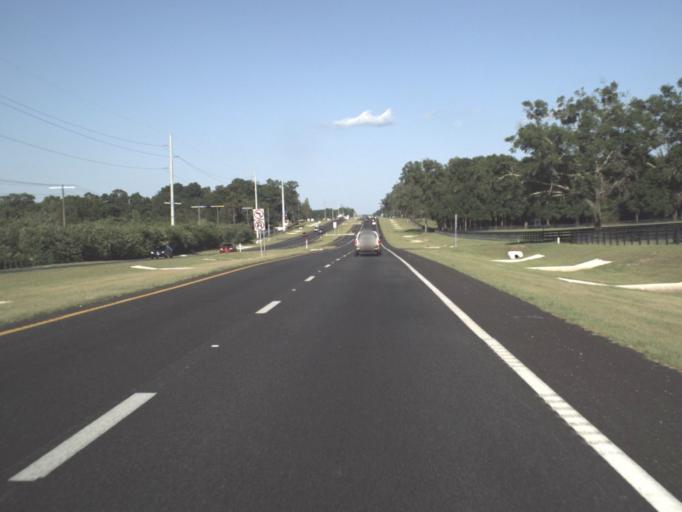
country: US
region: Florida
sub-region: Marion County
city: Ocala
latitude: 29.1868
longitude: -82.2679
